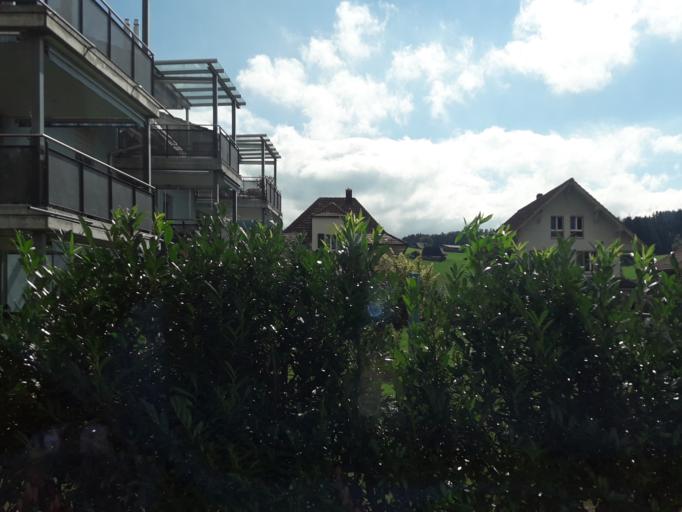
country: CH
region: Bern
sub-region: Bern-Mittelland District
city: Koniz
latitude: 46.8856
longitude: 7.3860
